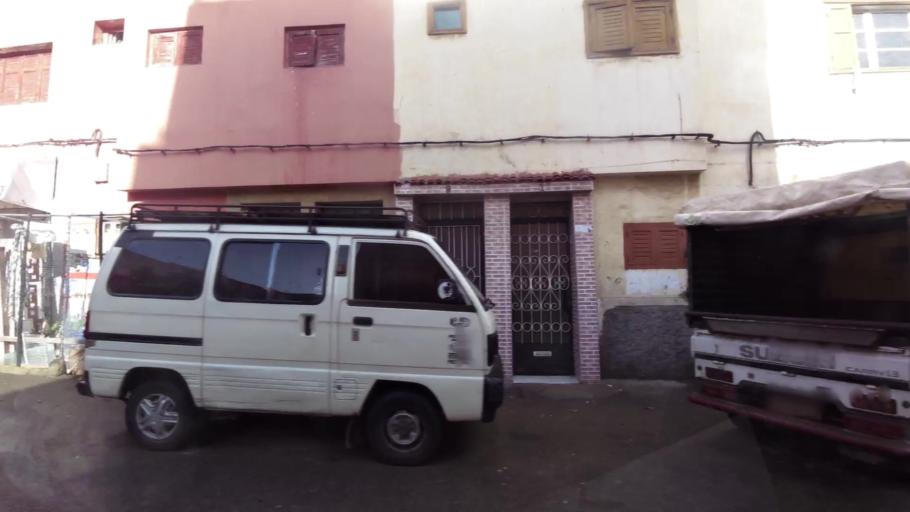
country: MA
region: Grand Casablanca
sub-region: Casablanca
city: Casablanca
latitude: 33.5574
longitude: -7.6862
